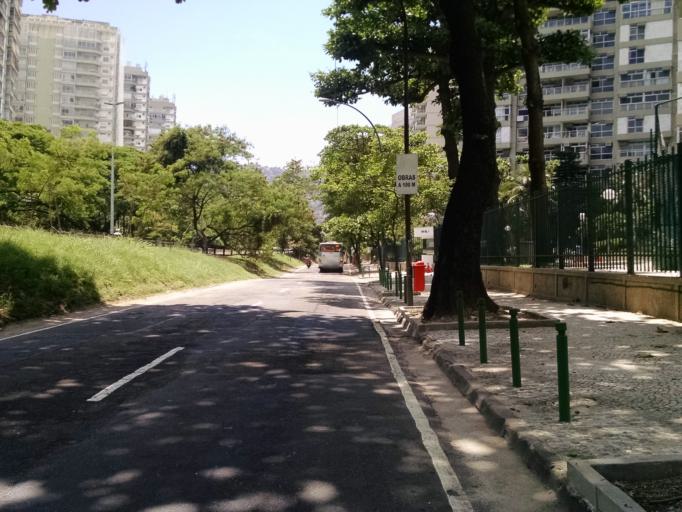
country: BR
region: Rio de Janeiro
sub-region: Rio De Janeiro
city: Rio de Janeiro
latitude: -22.9945
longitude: -43.2561
